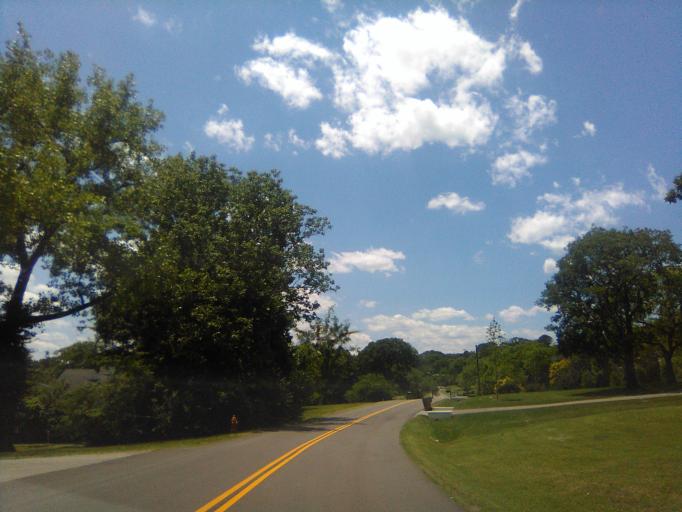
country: US
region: Tennessee
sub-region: Davidson County
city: Belle Meade
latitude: 36.1264
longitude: -86.8655
